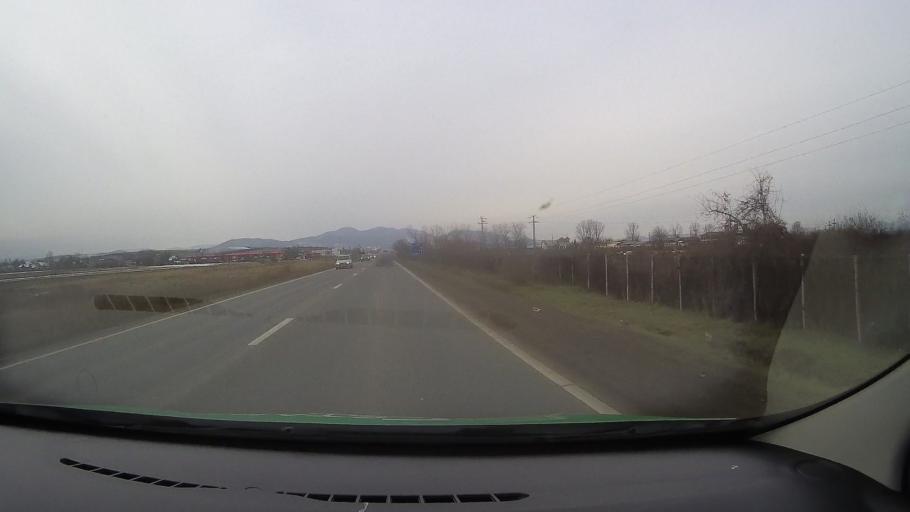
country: RO
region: Hunedoara
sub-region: Municipiul Deva
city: Cristur
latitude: 45.8523
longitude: 22.9705
